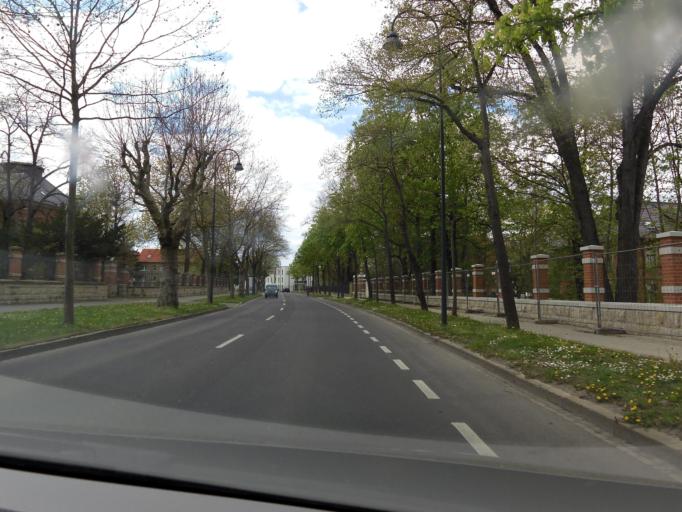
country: DE
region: Saxony-Anhalt
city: Naumburg
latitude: 51.1526
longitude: 11.7901
